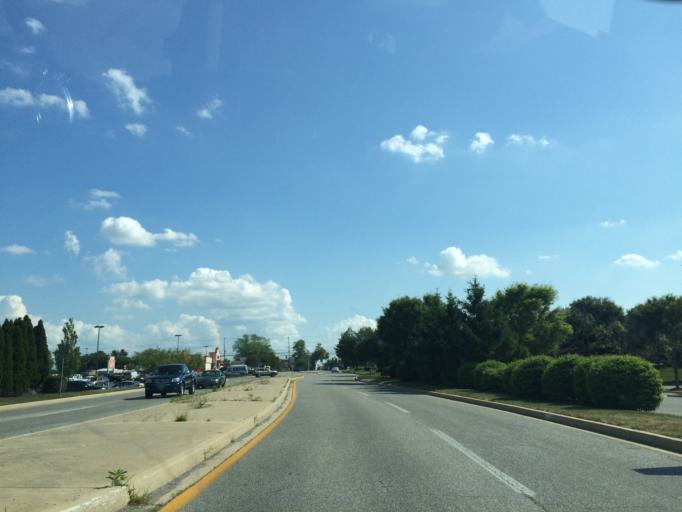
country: US
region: Maryland
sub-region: Carroll County
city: Eldersburg
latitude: 39.4046
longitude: -76.9439
